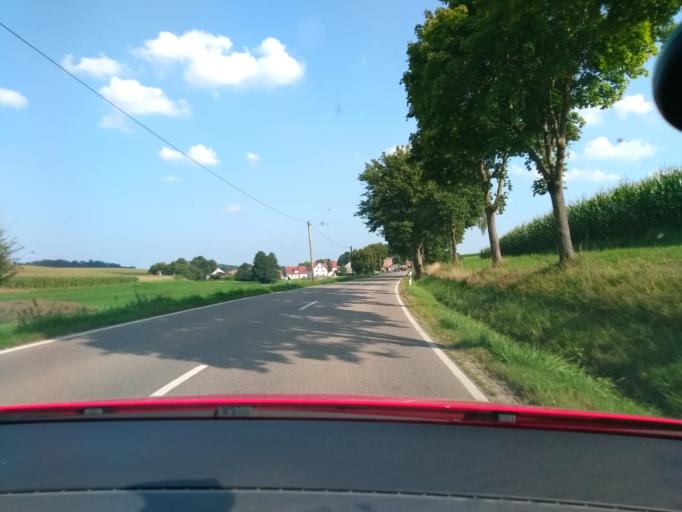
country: DE
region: Bavaria
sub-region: Upper Bavaria
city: Schwabhausen
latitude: 48.3855
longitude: 11.3388
